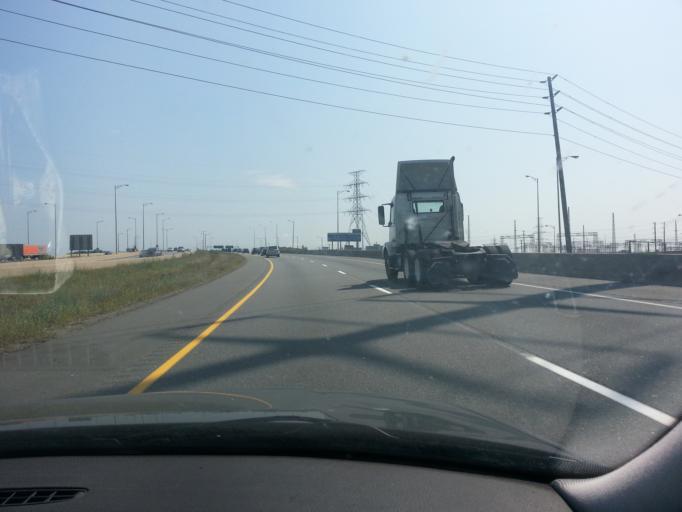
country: CA
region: Ontario
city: Burlington
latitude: 43.3342
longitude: -79.8294
